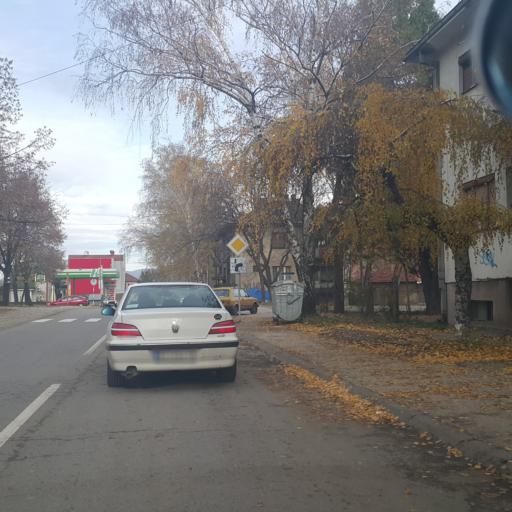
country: RS
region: Central Serbia
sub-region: Zajecarski Okrug
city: Knjazevac
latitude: 43.5708
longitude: 22.2517
